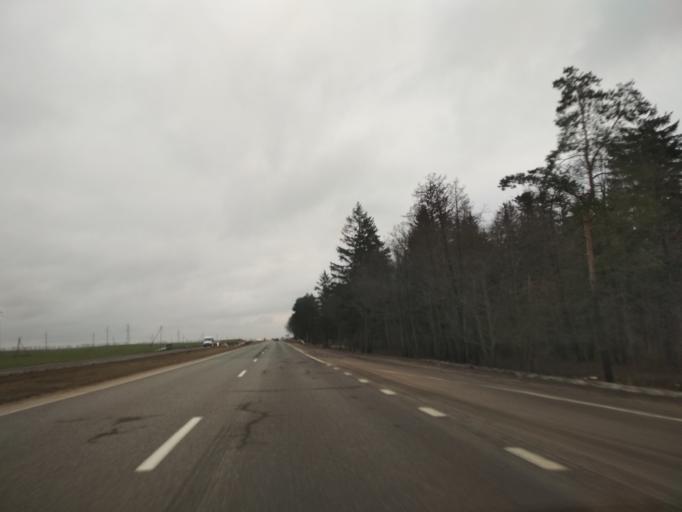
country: BY
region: Minsk
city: Mar''ina Horka
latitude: 53.6094
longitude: 28.0685
